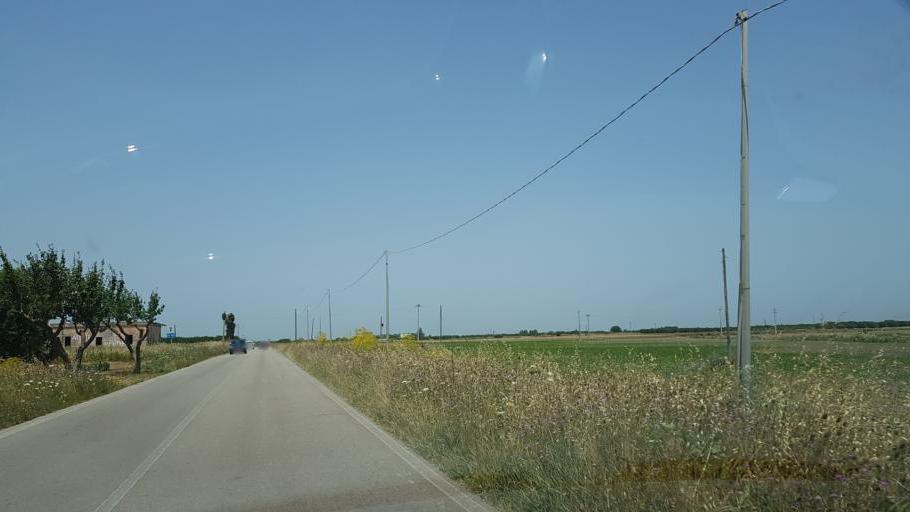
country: IT
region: Apulia
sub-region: Provincia di Brindisi
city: San Pancrazio Salentino
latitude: 40.3886
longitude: 17.8357
